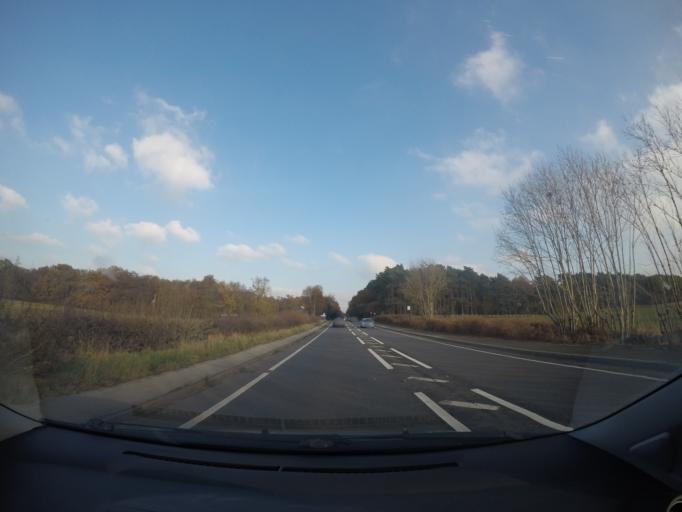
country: GB
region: England
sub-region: City of York
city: Holtby
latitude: 54.0170
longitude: -0.9804
